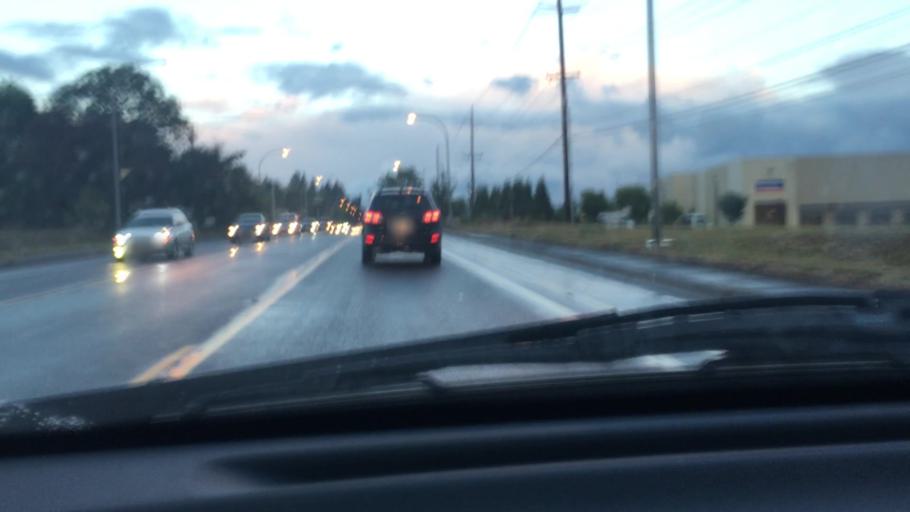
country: US
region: Oregon
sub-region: Washington County
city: King City
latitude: 45.3697
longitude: -122.8031
